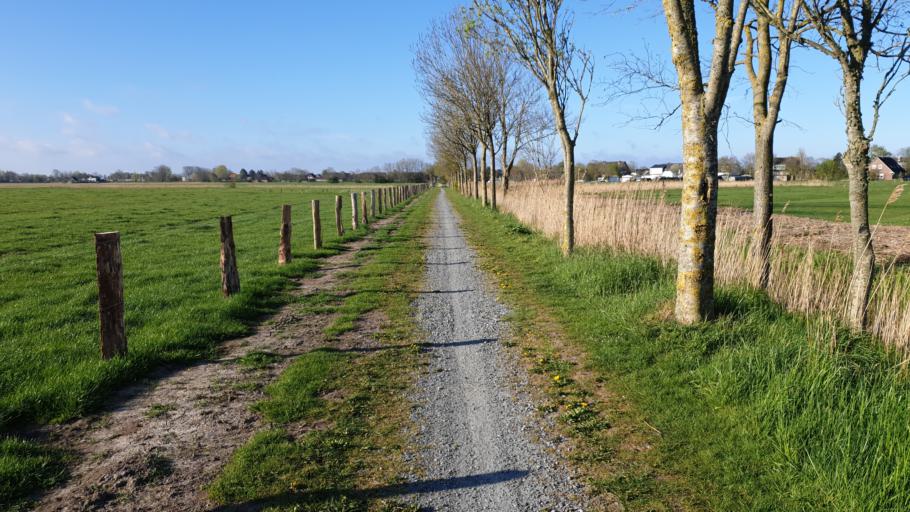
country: DE
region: Schleswig-Holstein
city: Elisabeth-Sophien-Koog
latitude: 54.4912
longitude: 8.8632
